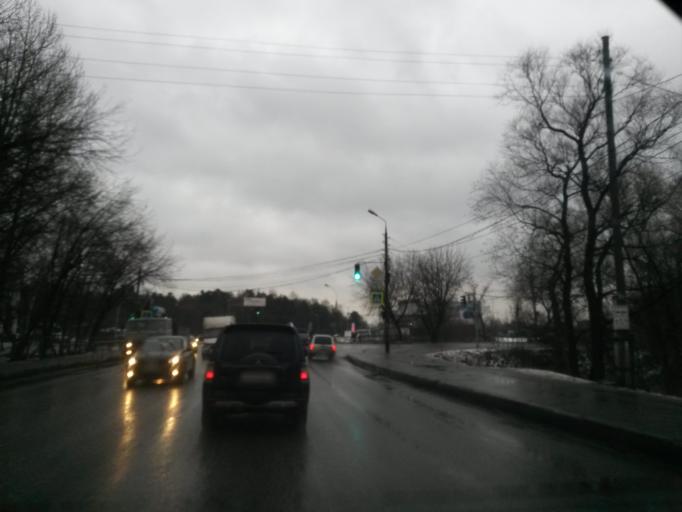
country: RU
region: Jaroslavl
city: Yaroslavl
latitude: 57.6440
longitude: 39.9166
